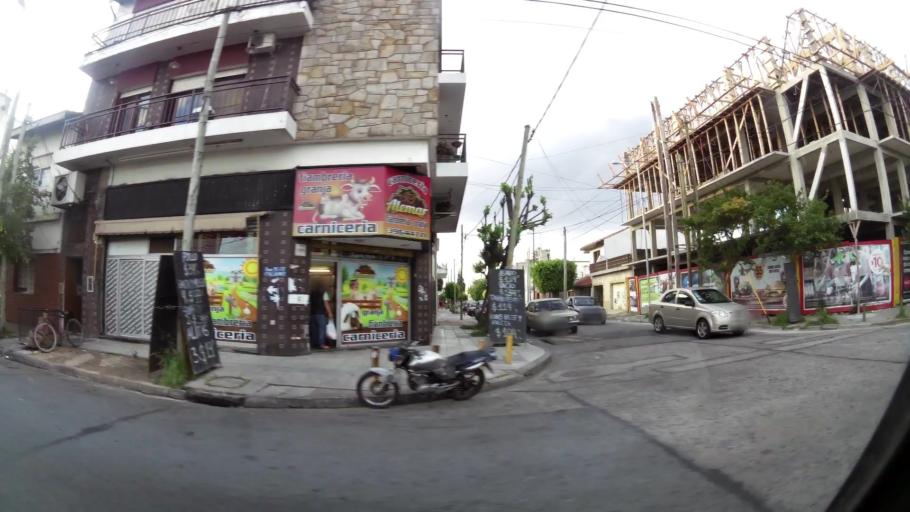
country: AR
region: Buenos Aires
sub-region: Partido de Avellaneda
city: Avellaneda
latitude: -34.6981
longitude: -58.3275
